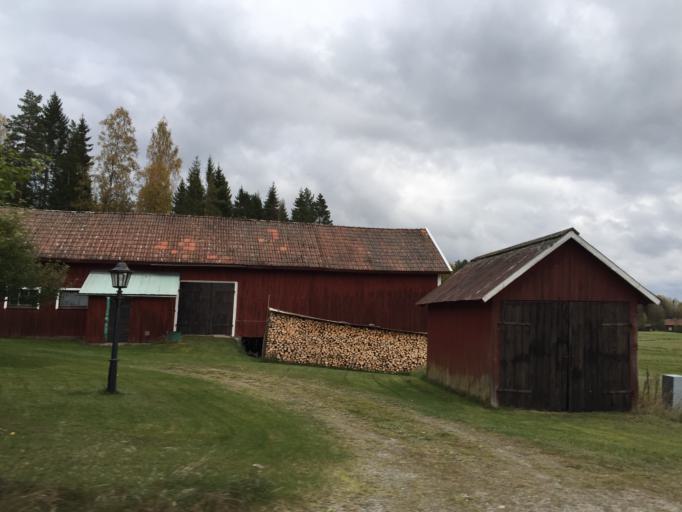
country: SE
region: Soedermanland
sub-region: Vingakers Kommun
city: Vingaker
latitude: 59.0251
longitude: 15.7777
